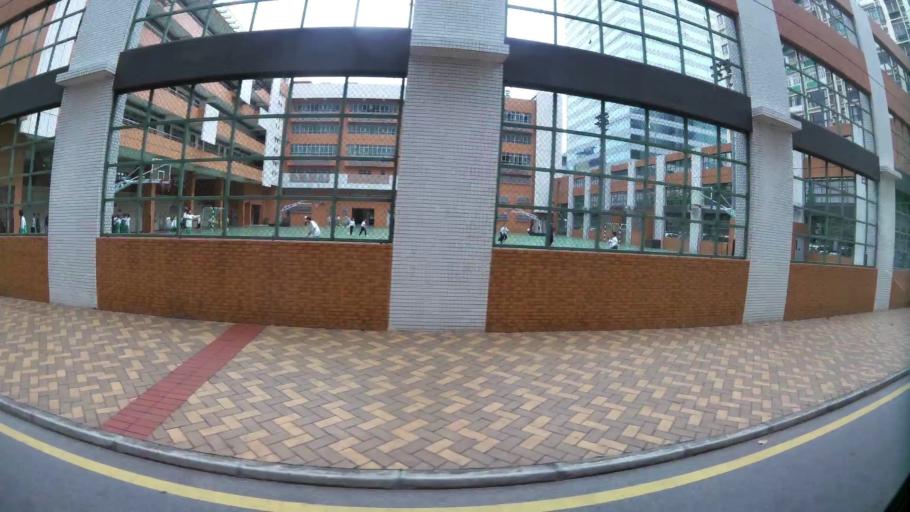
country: MO
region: Macau
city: Macau
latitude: 22.1891
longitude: 113.5526
